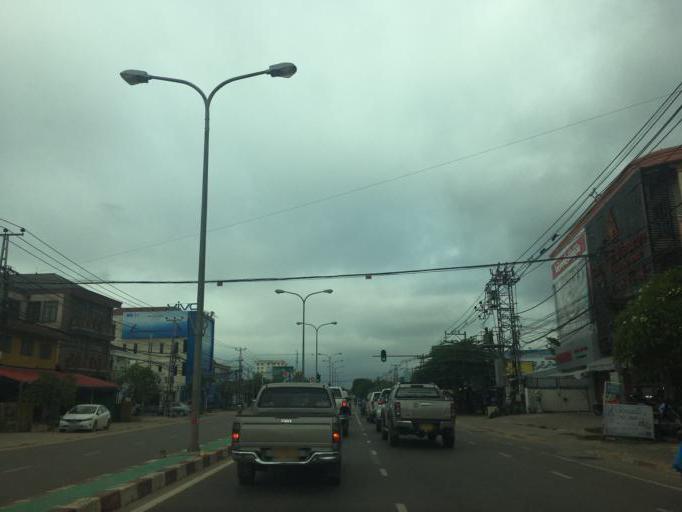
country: TH
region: Nong Khai
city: Si Chiang Mai
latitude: 17.9700
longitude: 102.5729
